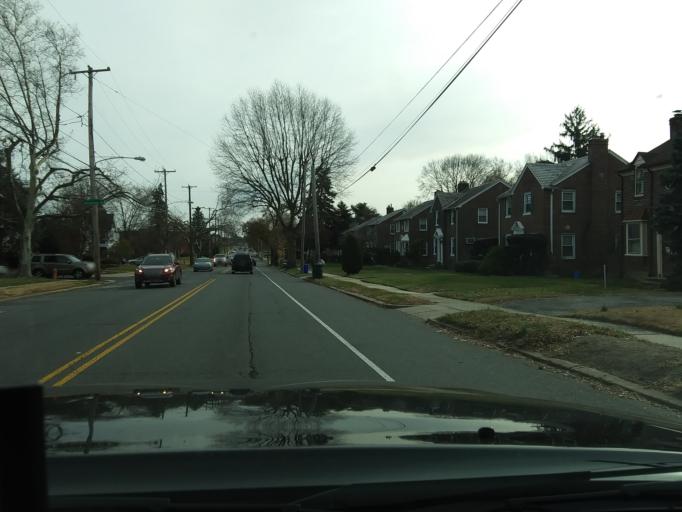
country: US
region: Pennsylvania
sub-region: Montgomery County
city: Rockledge
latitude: 40.0718
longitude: -75.0737
